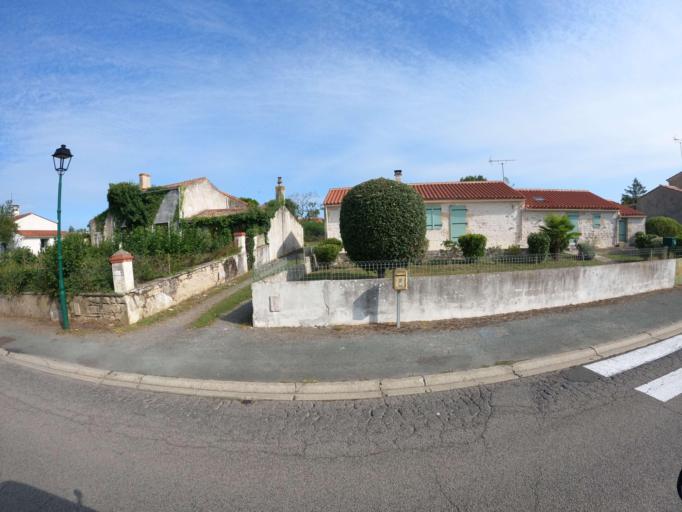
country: FR
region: Pays de la Loire
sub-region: Departement de la Vendee
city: Triaize
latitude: 46.3491
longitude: -1.2568
